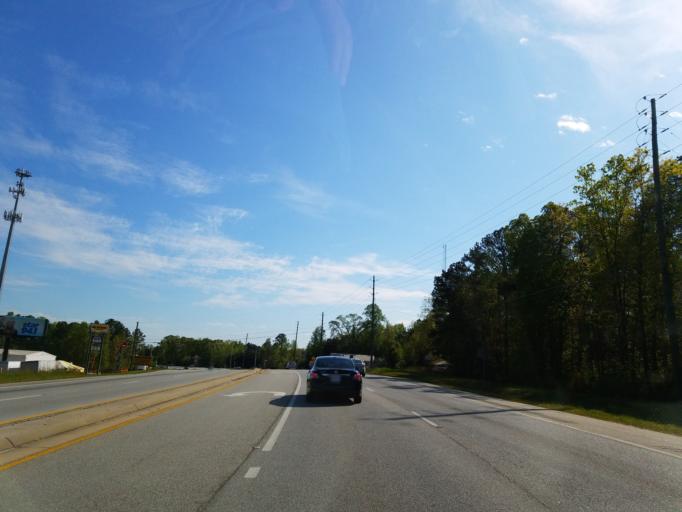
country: US
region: Georgia
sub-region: Douglas County
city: Lithia Springs
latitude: 33.7149
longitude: -84.6624
